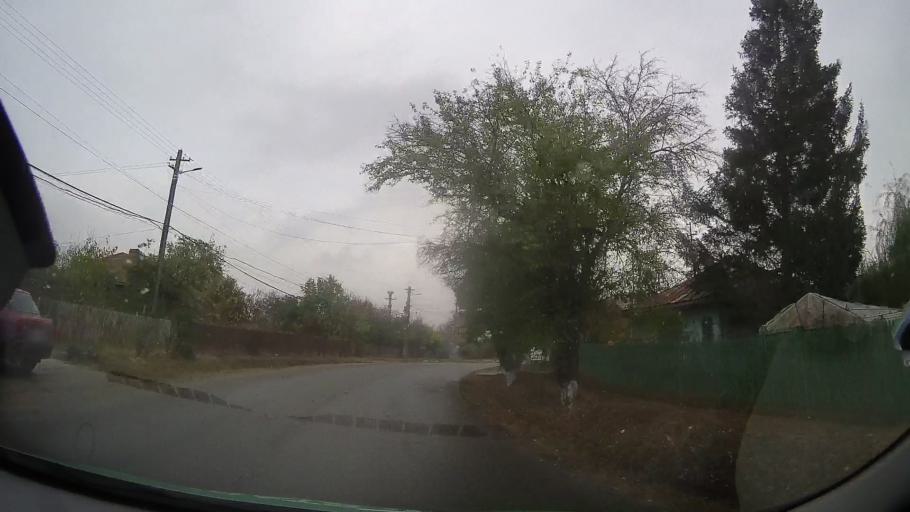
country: RO
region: Prahova
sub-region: Comuna Gherghita
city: Gherghita
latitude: 44.7993
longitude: 26.2846
